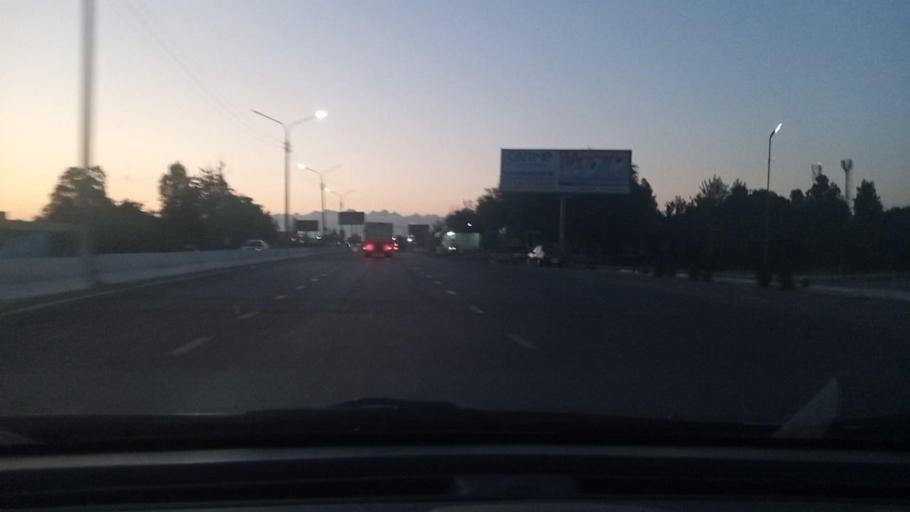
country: UZ
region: Toshkent Shahri
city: Tashkent
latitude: 41.2437
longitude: 69.2222
